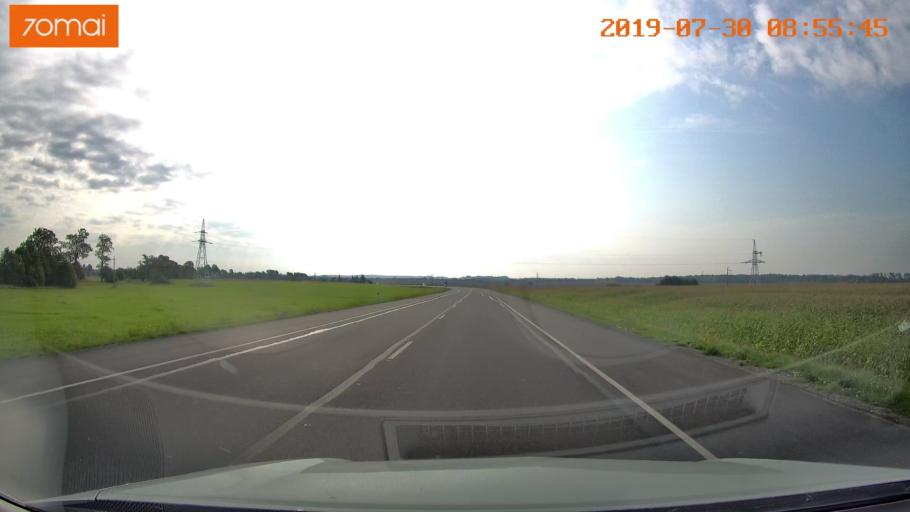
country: RU
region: Kaliningrad
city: Gusev
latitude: 54.5997
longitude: 22.0593
